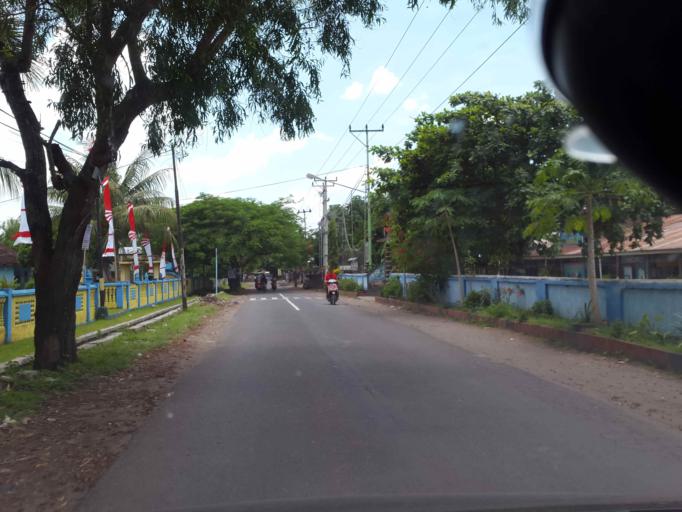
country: ID
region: West Nusa Tenggara
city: Mambalan
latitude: -8.5407
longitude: 116.1001
